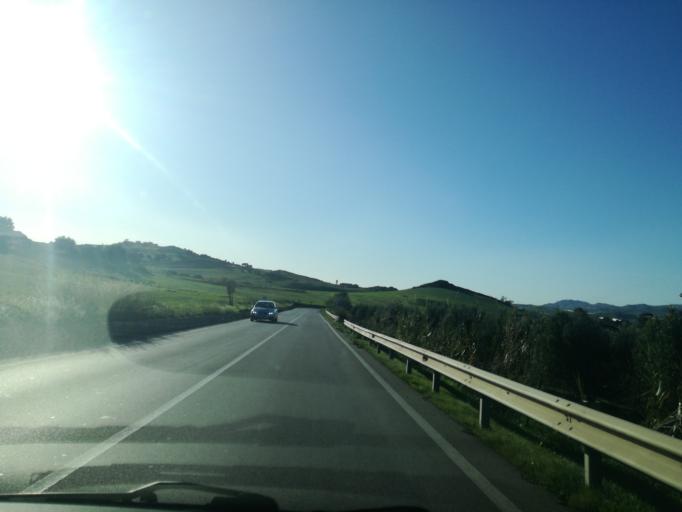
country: IT
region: Sicily
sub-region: Provincia di Caltanissetta
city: Butera
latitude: 37.1132
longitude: 14.1519
